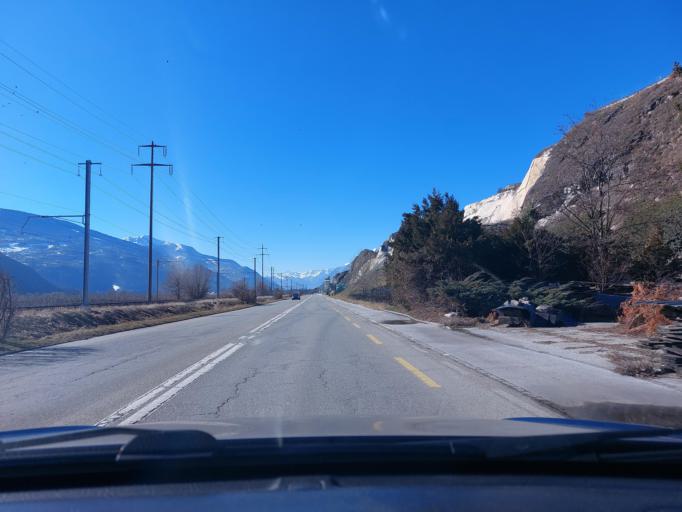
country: CH
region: Valais
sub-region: Sierre District
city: Grone
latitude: 46.2588
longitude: 7.4416
